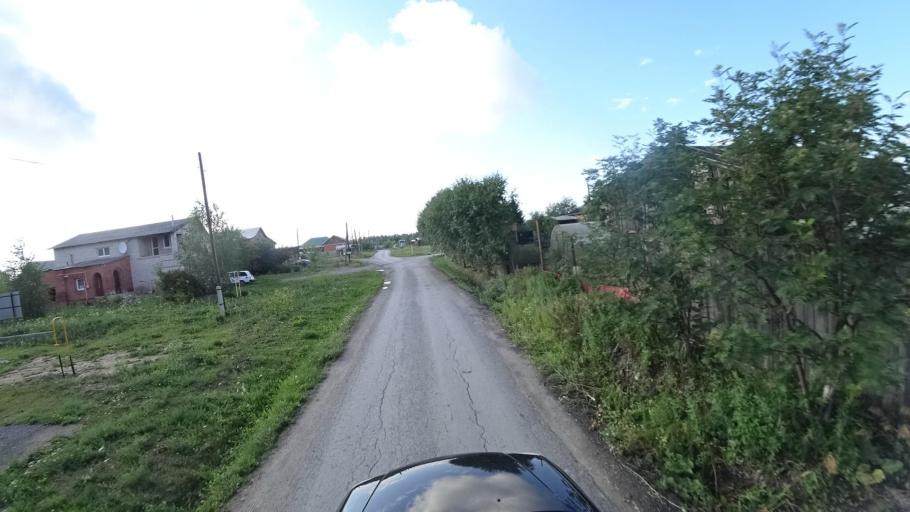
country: RU
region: Sverdlovsk
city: Obukhovskoye
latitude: 56.8495
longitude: 62.6532
